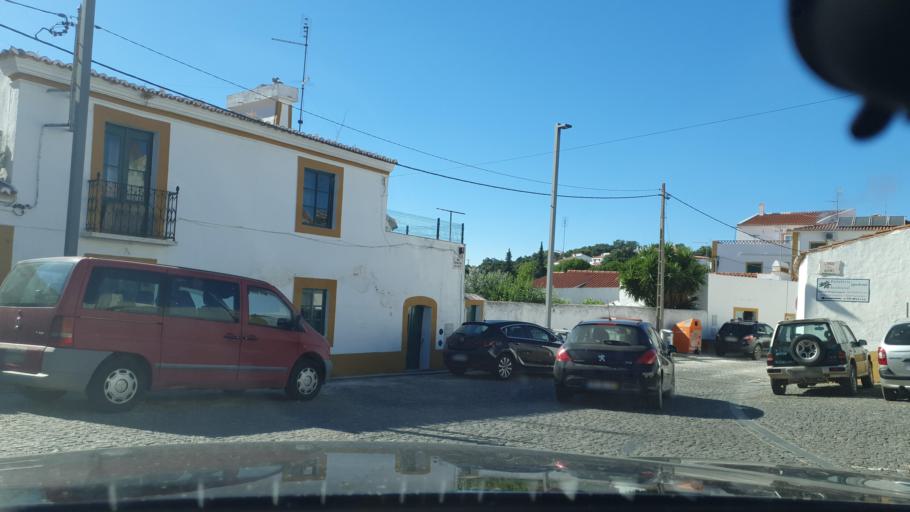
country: PT
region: Evora
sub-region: Alandroal
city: Alandroal
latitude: 38.7023
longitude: -7.4039
